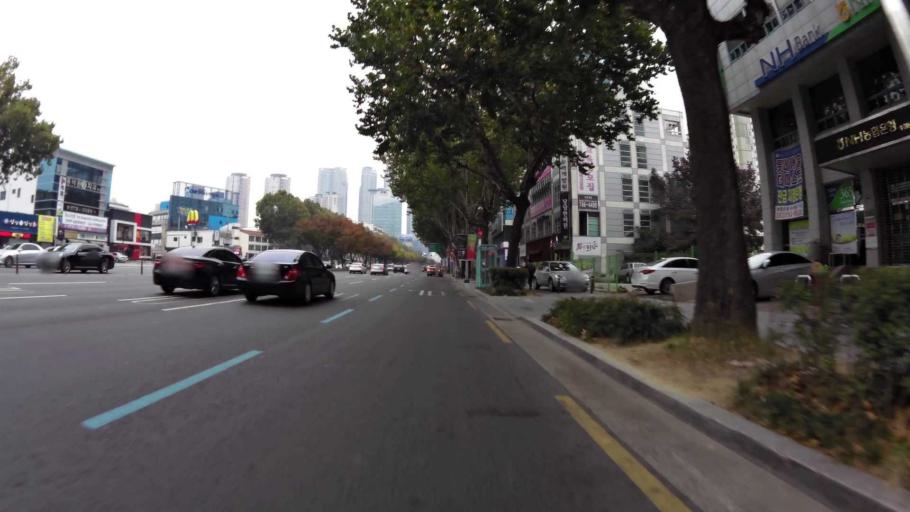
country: KR
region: Daegu
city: Daegu
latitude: 35.8594
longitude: 128.6183
